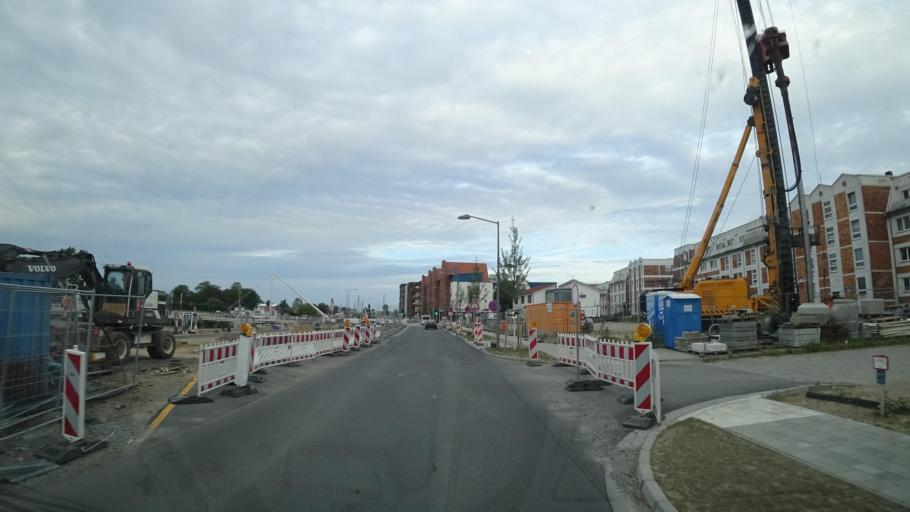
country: DE
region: Mecklenburg-Vorpommern
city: Greifswald
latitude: 54.0987
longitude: 13.3810
